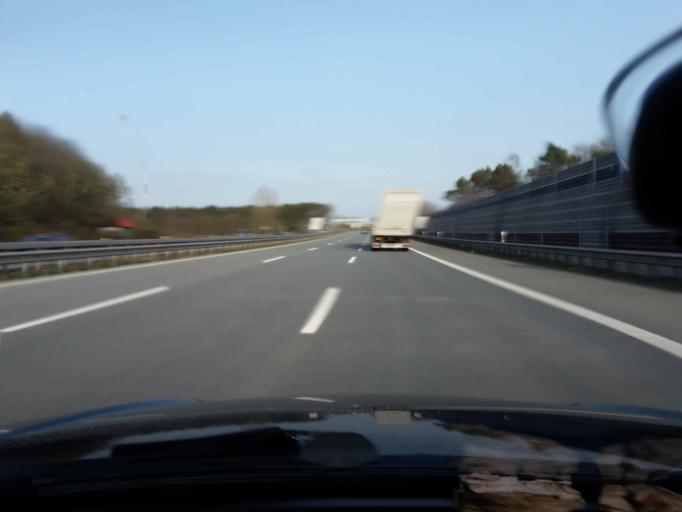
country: DE
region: Lower Saxony
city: Buchholz in der Nordheide
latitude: 53.3727
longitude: 9.8564
